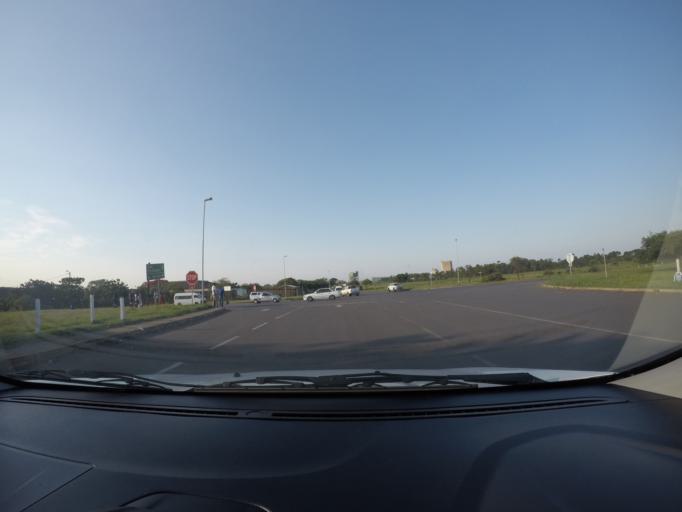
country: ZA
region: KwaZulu-Natal
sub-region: uThungulu District Municipality
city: Richards Bay
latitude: -28.7680
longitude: 32.0096
